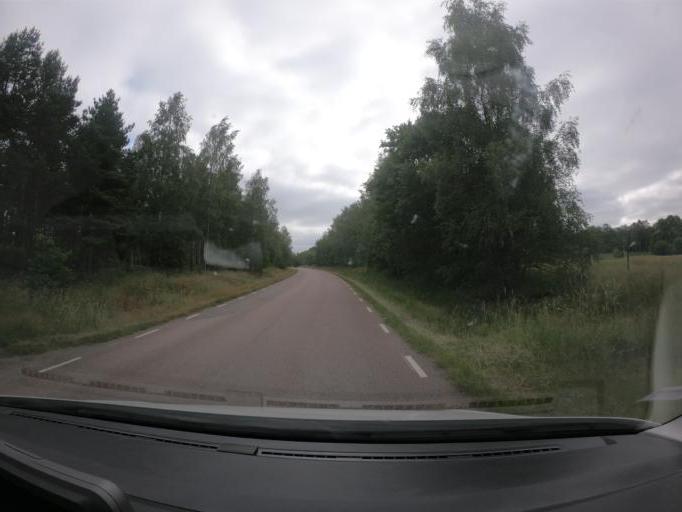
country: SE
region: Skane
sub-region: Klippans Kommun
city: Ljungbyhed
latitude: 56.0300
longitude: 13.3337
